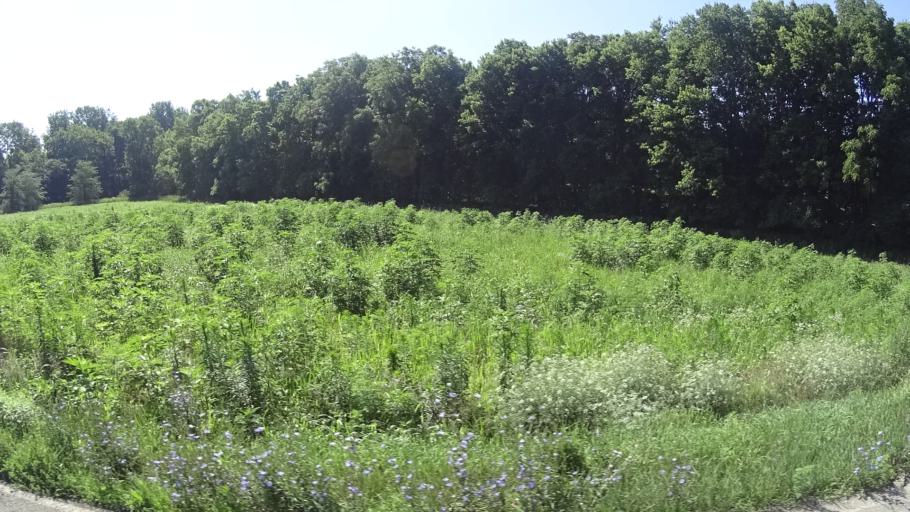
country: US
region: Indiana
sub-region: Madison County
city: Pendleton
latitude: 39.9950
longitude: -85.7577
